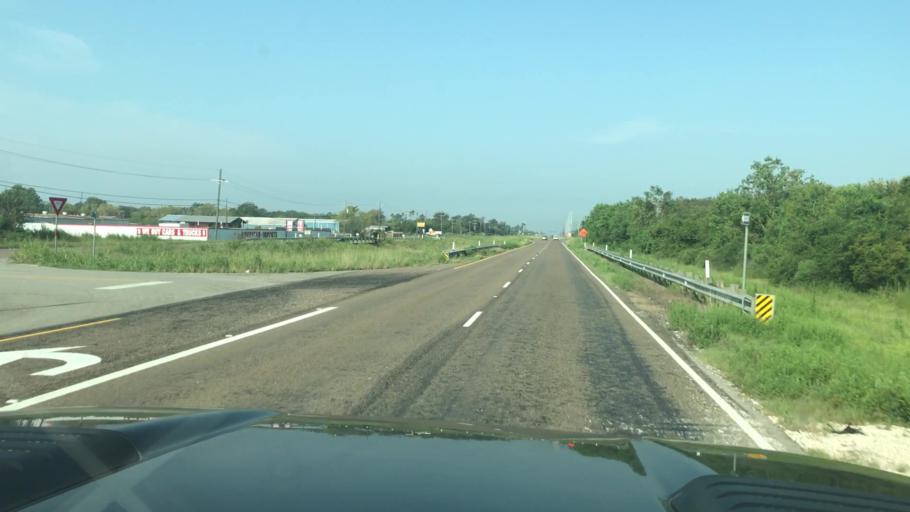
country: US
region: Texas
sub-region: Jefferson County
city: Bevil Oaks
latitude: 30.0640
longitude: -94.2167
